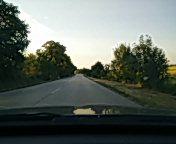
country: HU
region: Fejer
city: Etyek
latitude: 47.4997
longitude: 18.7604
